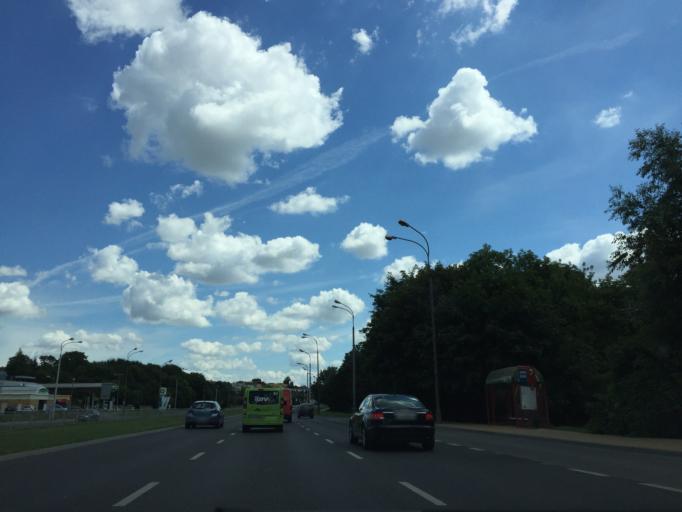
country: PL
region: Lublin Voivodeship
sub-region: Powiat lubelski
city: Lublin
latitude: 51.2531
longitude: 22.5538
